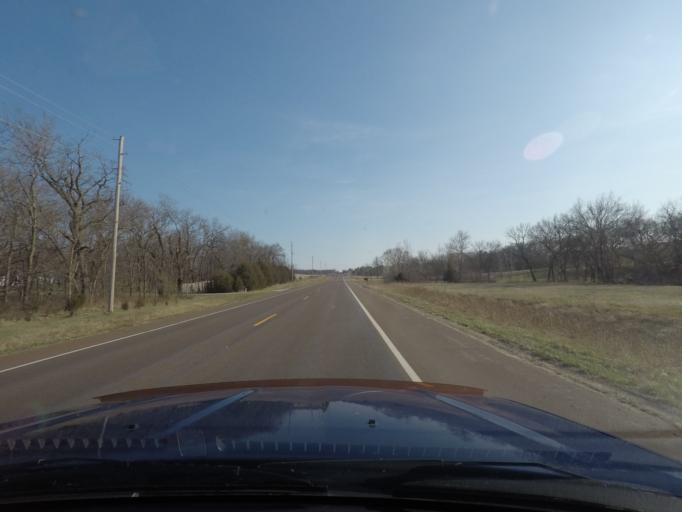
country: US
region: Kansas
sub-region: Douglas County
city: Lawrence
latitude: 39.0092
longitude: -95.3914
